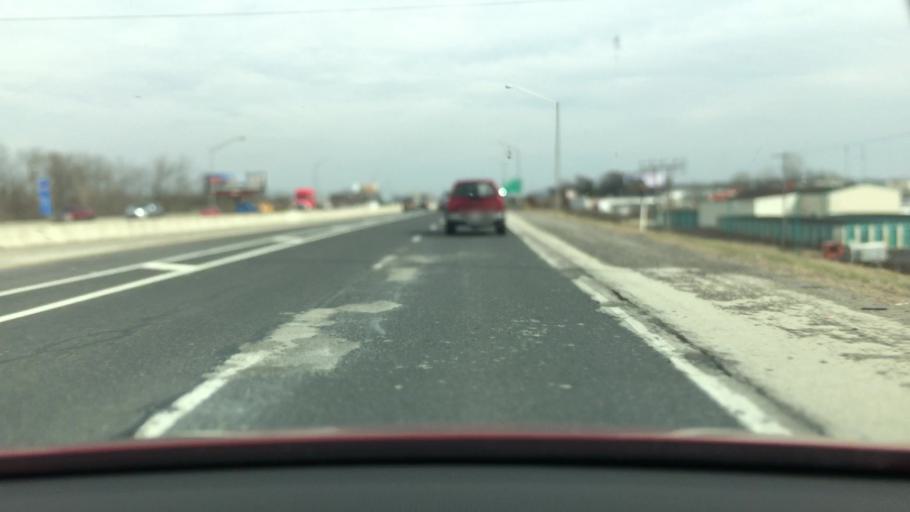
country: US
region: Indiana
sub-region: Boone County
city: Zionsville
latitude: 39.9276
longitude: -86.2594
